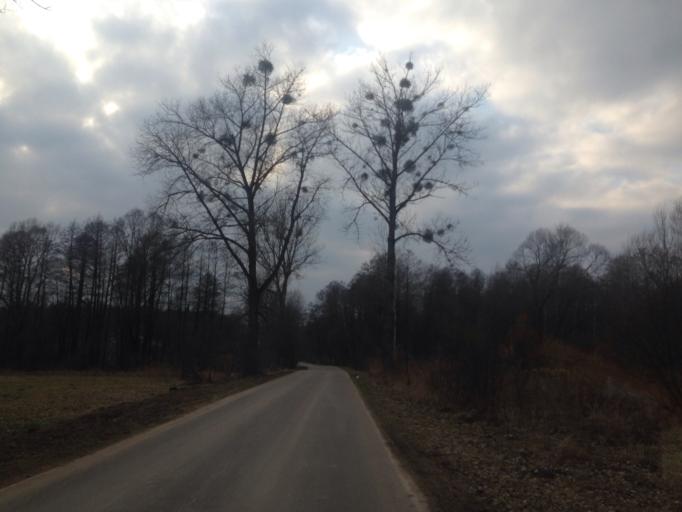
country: PL
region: Warmian-Masurian Voivodeship
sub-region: Powiat dzialdowski
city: Lidzbark
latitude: 53.3484
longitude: 19.7492
